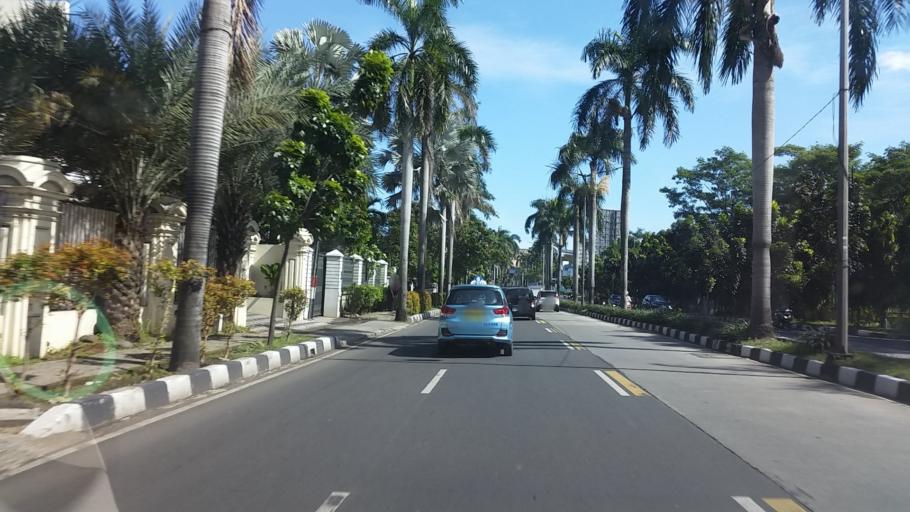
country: ID
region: Banten
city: South Tangerang
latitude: -6.2724
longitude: 106.7829
